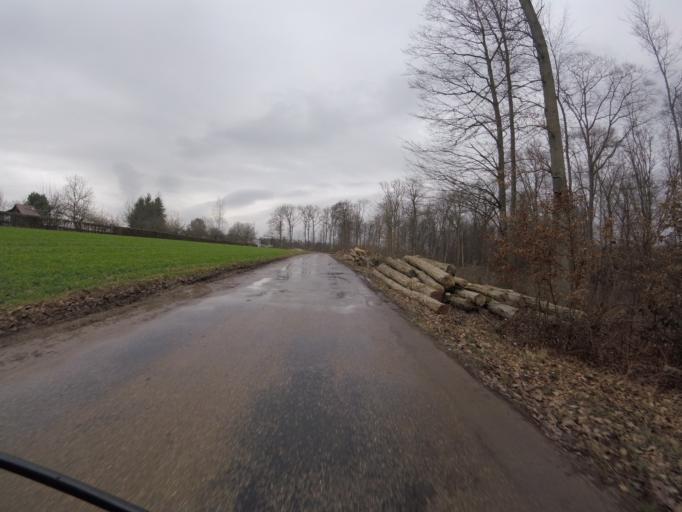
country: DE
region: Baden-Wuerttemberg
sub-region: Regierungsbezirk Stuttgart
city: Backnang
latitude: 48.9592
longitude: 9.4437
